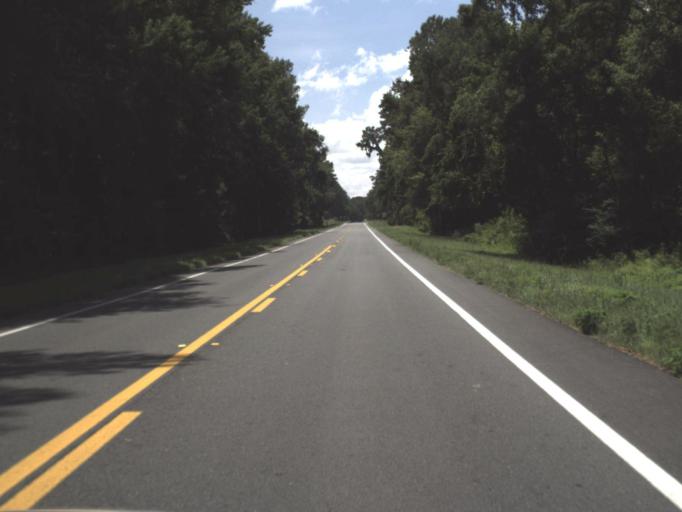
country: US
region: Florida
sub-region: Suwannee County
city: Wellborn
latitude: 30.3469
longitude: -82.7691
